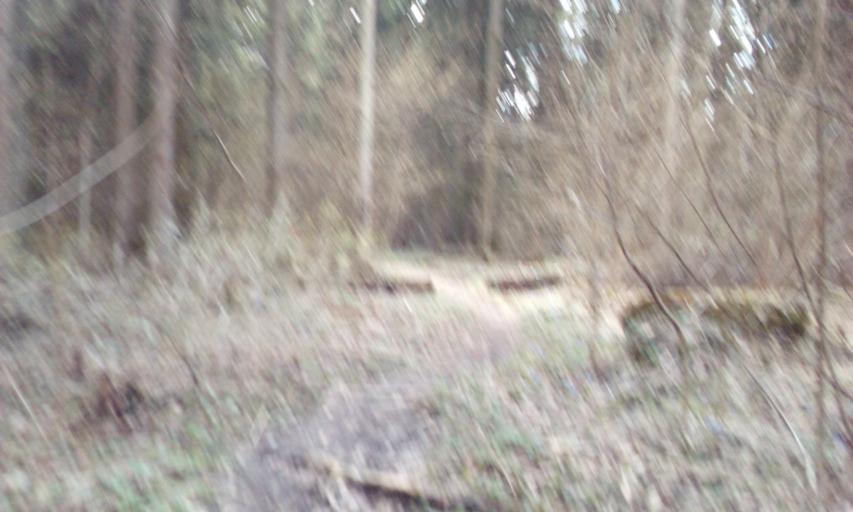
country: RU
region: Moskovskaya
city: Lesnoy Gorodok
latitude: 55.6392
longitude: 37.2505
